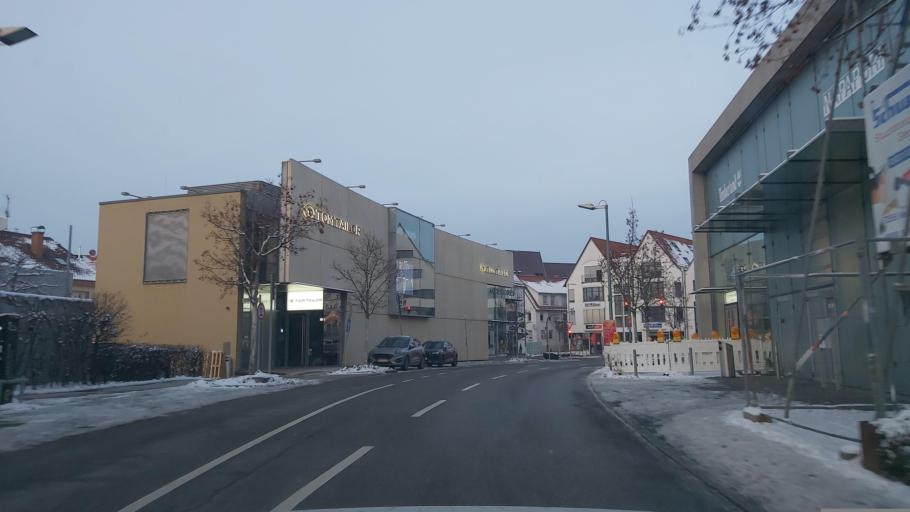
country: DE
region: Baden-Wuerttemberg
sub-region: Tuebingen Region
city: Metzingen
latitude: 48.5370
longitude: 9.2816
